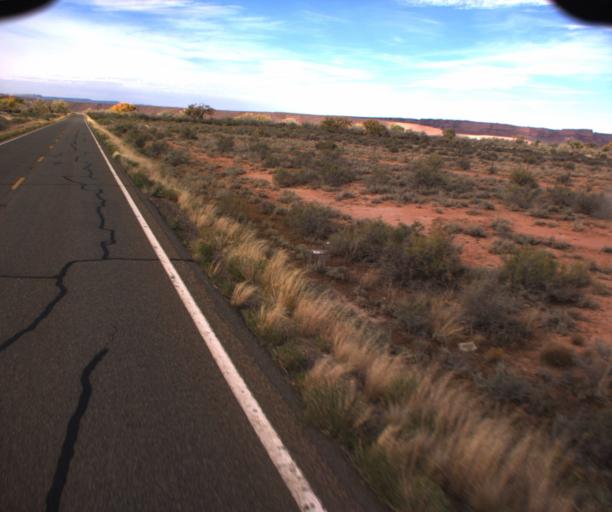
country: US
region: Arizona
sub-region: Apache County
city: Many Farms
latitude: 36.4655
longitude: -109.5843
